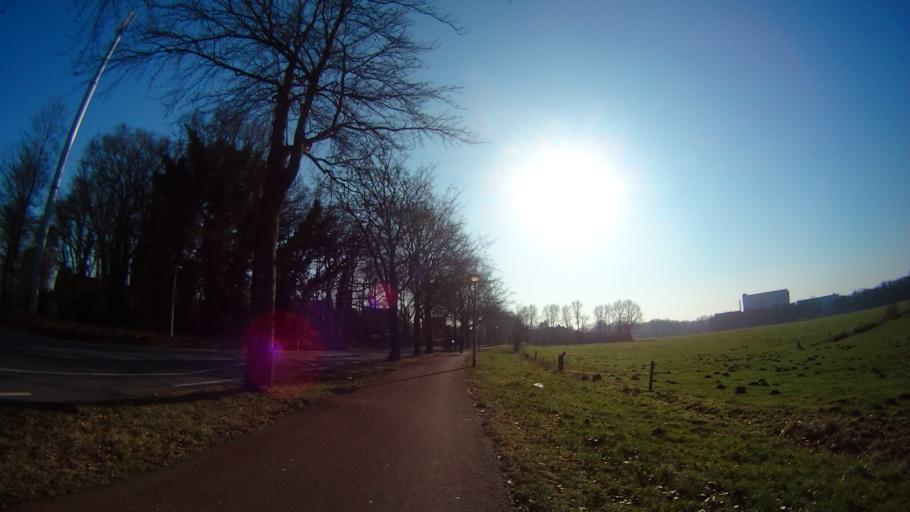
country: NL
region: Utrecht
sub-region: Gemeente Amersfoort
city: Hoogland
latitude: 52.1736
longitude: 5.3763
